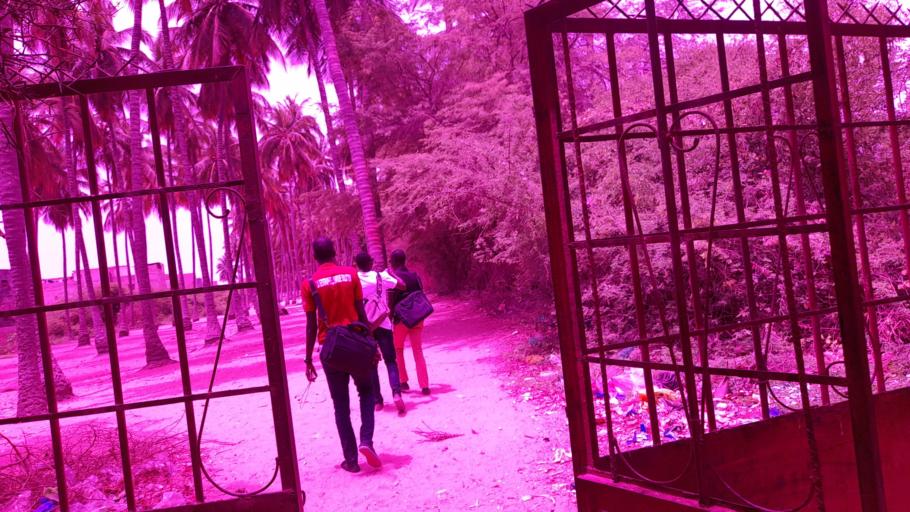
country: SN
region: Saint-Louis
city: Saint-Louis
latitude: 16.0164
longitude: -16.4874
